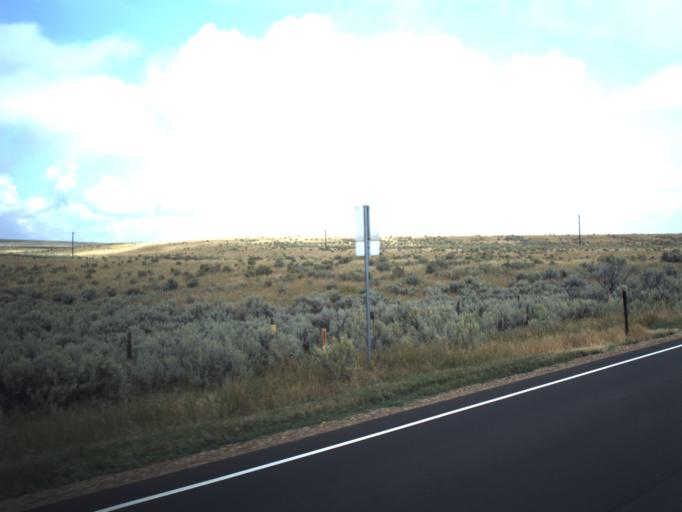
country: US
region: Utah
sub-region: Rich County
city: Randolph
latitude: 41.6855
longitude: -111.1784
